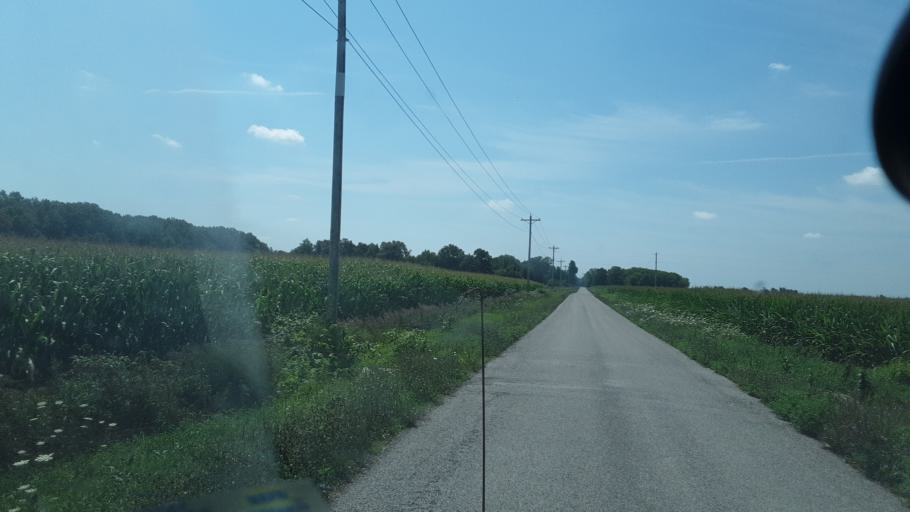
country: US
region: Ohio
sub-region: Hancock County
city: Findlay
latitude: 40.9728
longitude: -83.5553
